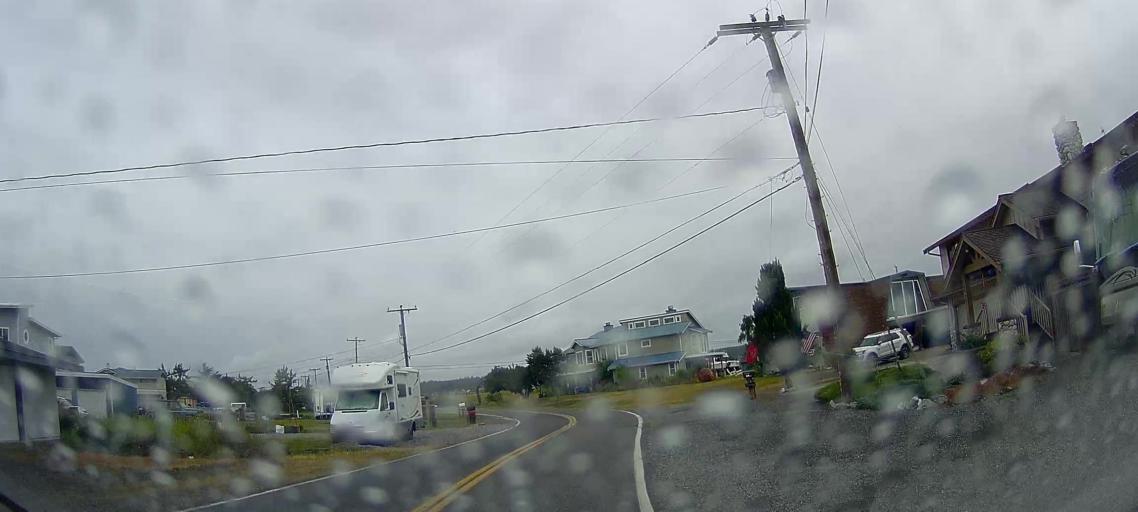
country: US
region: Washington
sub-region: Whatcom County
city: Marietta
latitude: 48.7905
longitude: -122.7102
